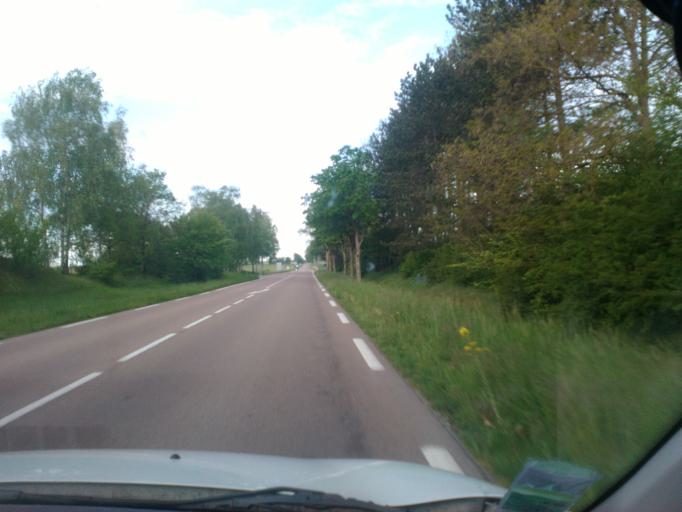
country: FR
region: Champagne-Ardenne
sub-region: Departement de l'Aube
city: Bar-sur-Aube
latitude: 48.2661
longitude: 4.6075
